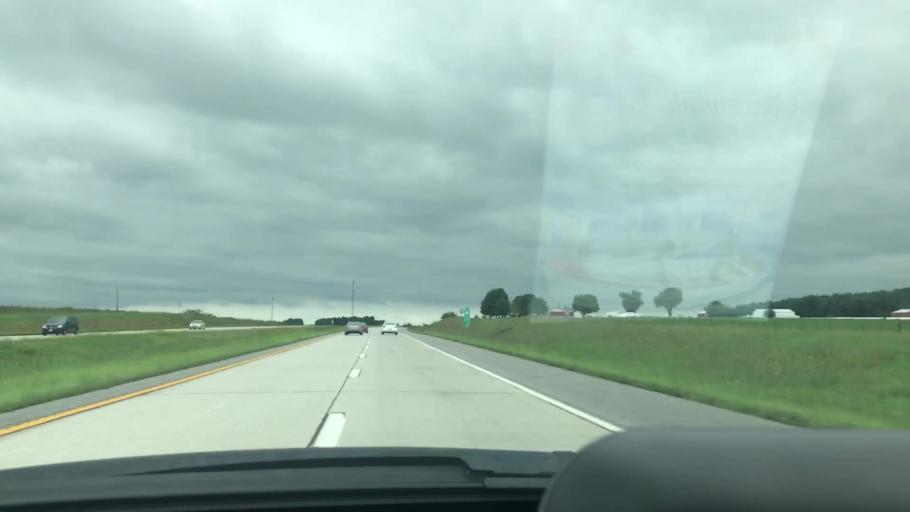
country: US
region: Missouri
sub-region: Greene County
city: Fair Grove
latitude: 37.4424
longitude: -93.1442
